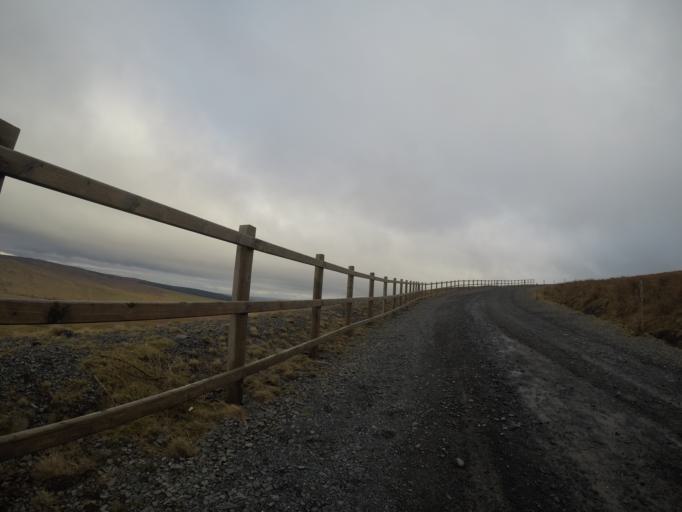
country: GB
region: Scotland
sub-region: North Ayrshire
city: Fairlie
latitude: 55.7633
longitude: -4.7932
